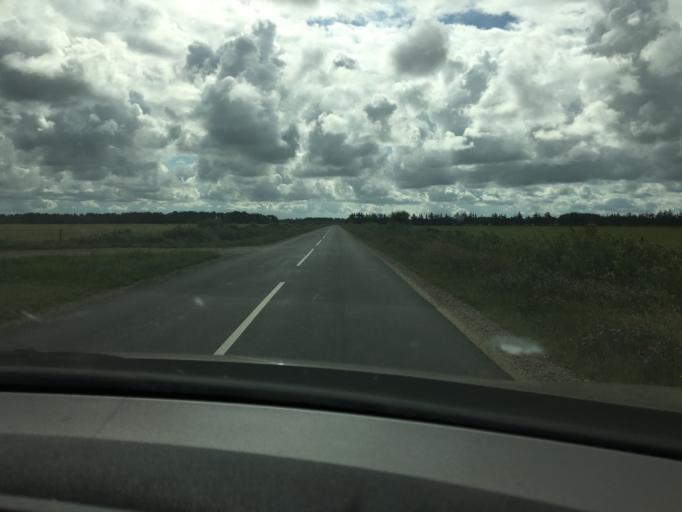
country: DK
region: Central Jutland
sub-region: Ringkobing-Skjern Kommune
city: Hvide Sande
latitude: 55.8311
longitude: 8.2170
